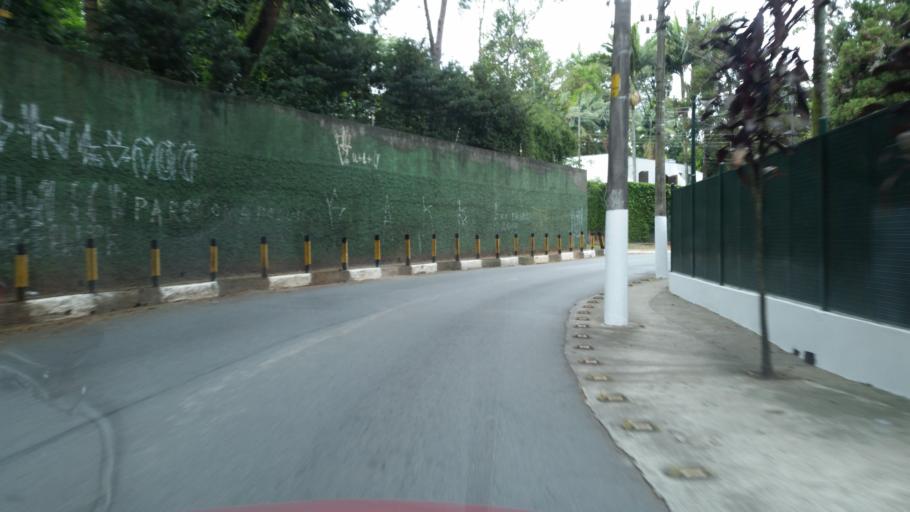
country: BR
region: Sao Paulo
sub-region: Diadema
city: Diadema
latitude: -23.6493
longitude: -46.6881
